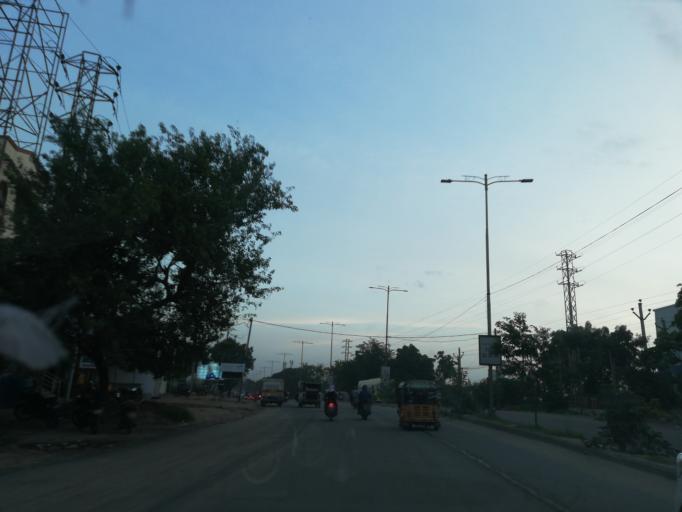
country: IN
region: Telangana
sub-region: Medak
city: Serilingampalle
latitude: 17.5334
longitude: 78.3570
